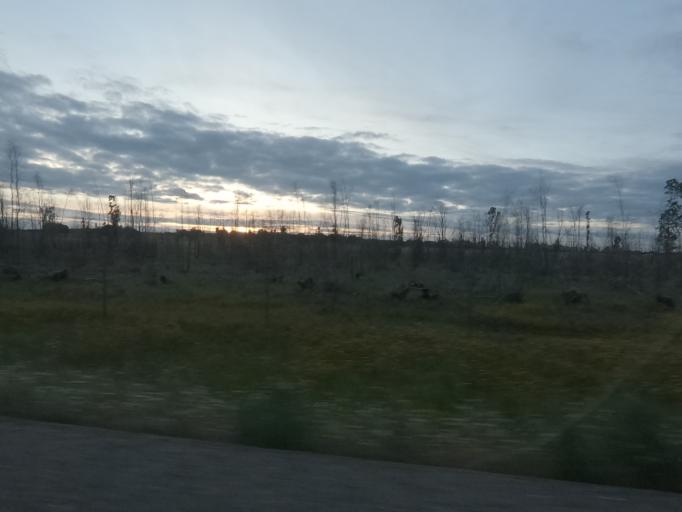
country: ES
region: Extremadura
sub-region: Provincia de Badajoz
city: Badajoz
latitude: 38.9781
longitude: -6.8866
